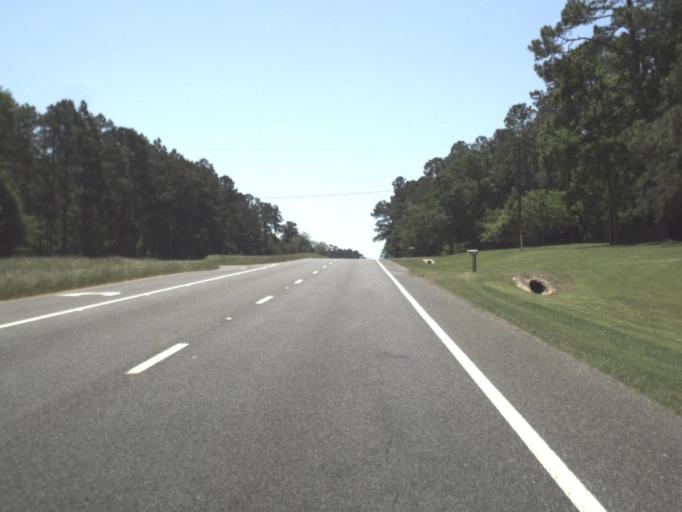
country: US
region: Florida
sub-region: Jefferson County
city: Monticello
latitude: 30.5986
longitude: -83.8714
